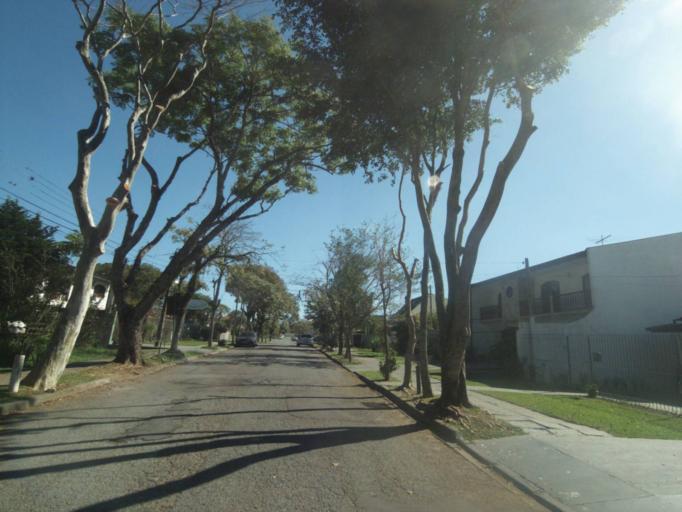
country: BR
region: Parana
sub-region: Curitiba
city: Curitiba
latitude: -25.3896
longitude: -49.2327
